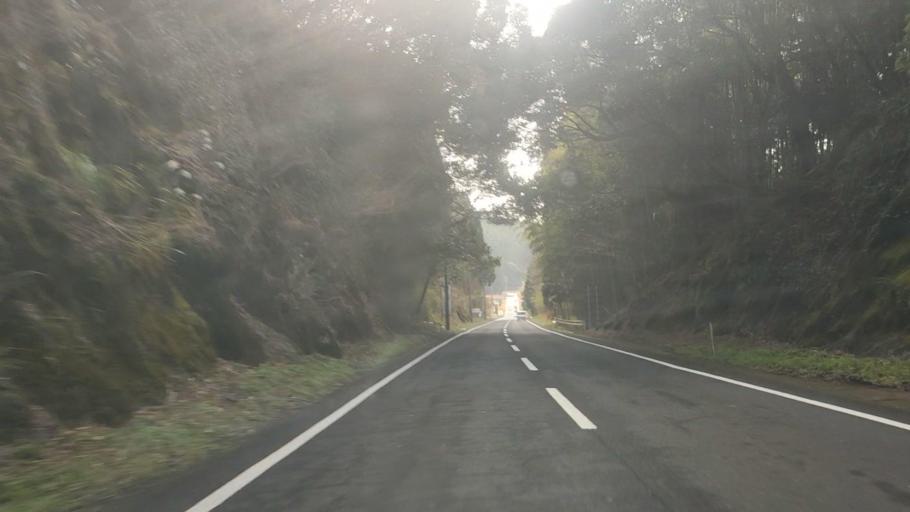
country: JP
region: Kagoshima
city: Okuchi-shinohara
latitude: 31.9669
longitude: 130.7395
